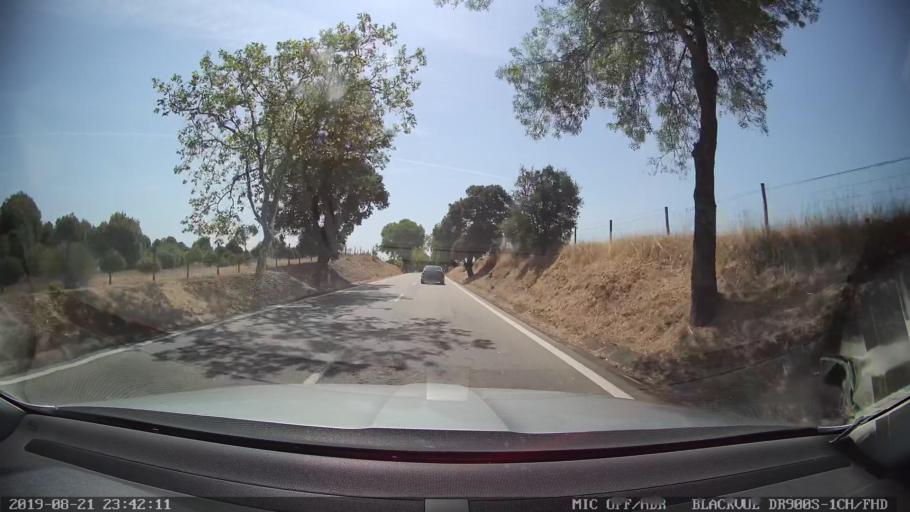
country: PT
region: Castelo Branco
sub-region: Idanha-A-Nova
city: Idanha-a-Nova
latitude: 39.8585
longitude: -7.3142
